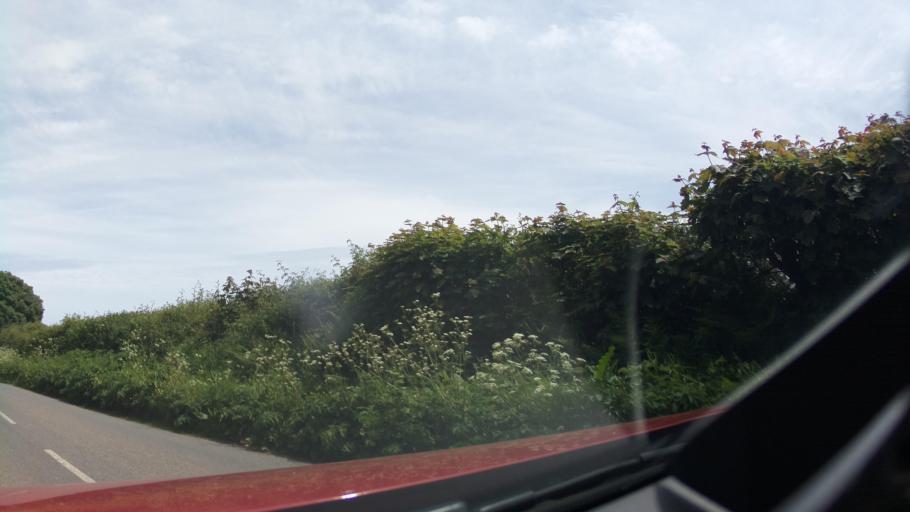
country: GB
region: England
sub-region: Devon
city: Kingsbridge
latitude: 50.3602
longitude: -3.7481
